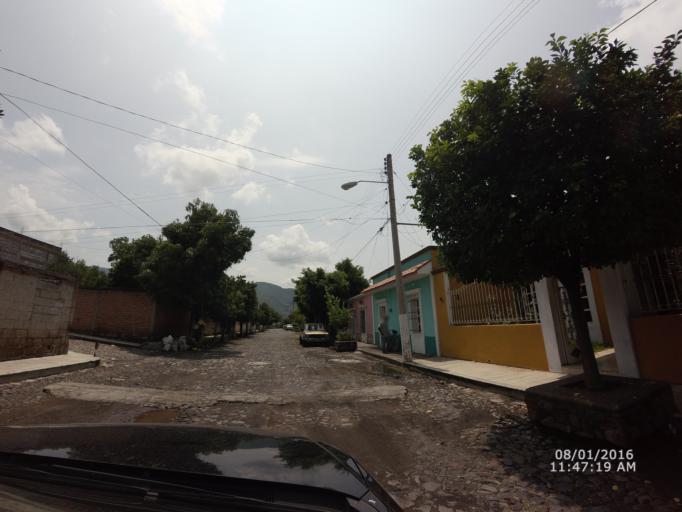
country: MX
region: Nayarit
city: Jala
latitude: 21.1039
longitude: -104.4433
